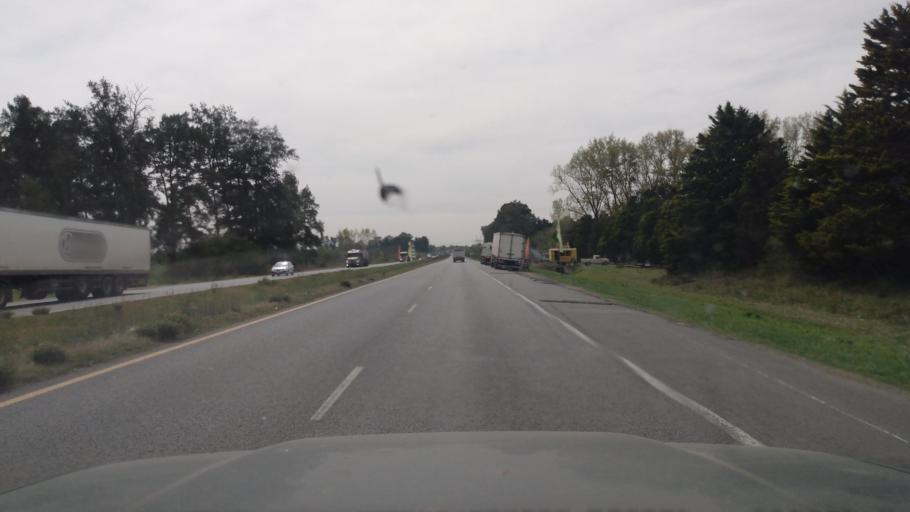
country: AR
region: Buenos Aires
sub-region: Partido de Lujan
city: Lujan
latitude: -34.4606
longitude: -59.0608
